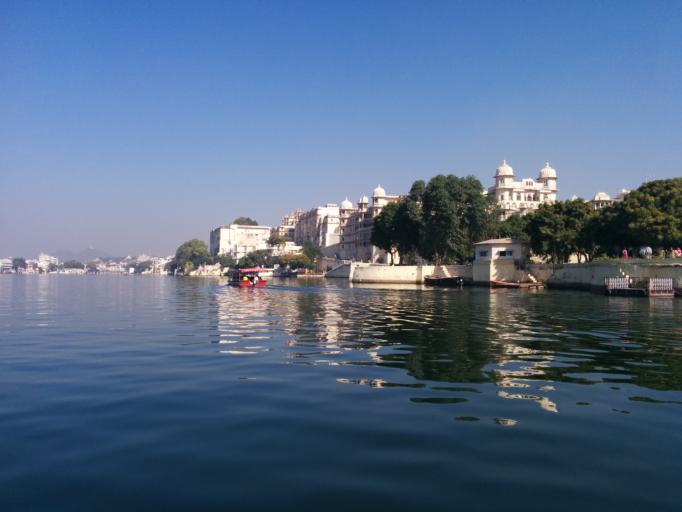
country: IN
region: Rajasthan
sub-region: Udaipur
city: Udaipur
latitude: 24.5726
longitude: 73.6825
